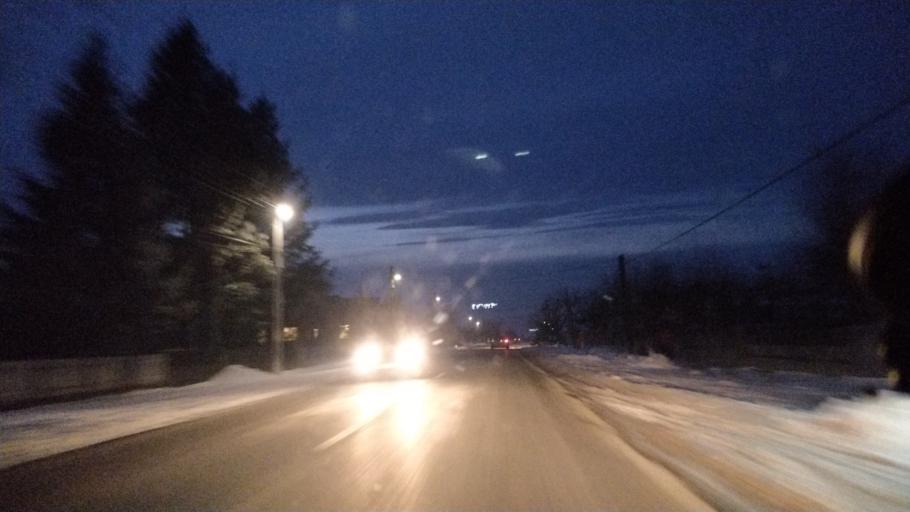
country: RO
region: Vrancea
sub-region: Comuna Rastoaca
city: Rastoaca
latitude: 45.6657
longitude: 27.2704
